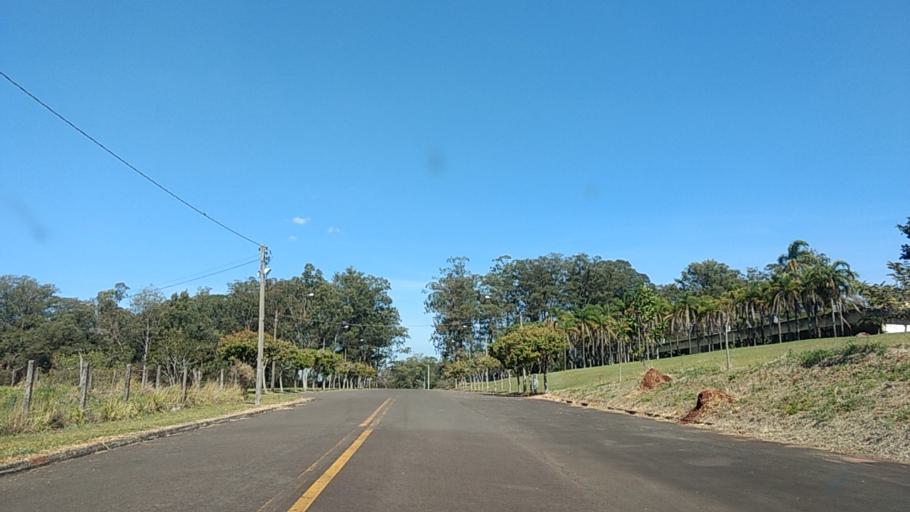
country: BR
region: Sao Paulo
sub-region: Botucatu
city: Botucatu
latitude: -22.8470
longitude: -48.4326
